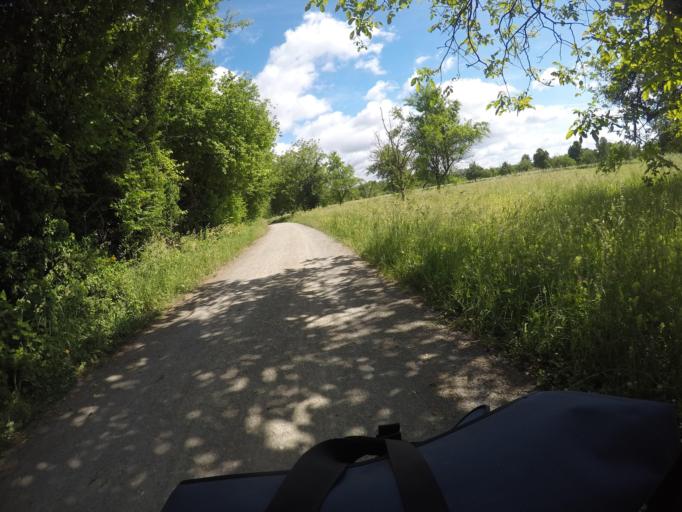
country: DE
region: Baden-Wuerttemberg
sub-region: Karlsruhe Region
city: Rheinstetten
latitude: 48.9804
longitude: 8.2816
